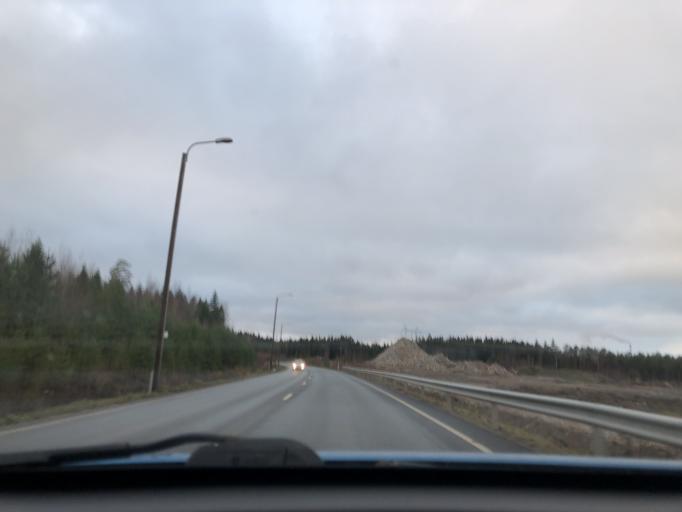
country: FI
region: Pirkanmaa
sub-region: Tampere
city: Kangasala
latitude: 61.5345
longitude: 23.9901
